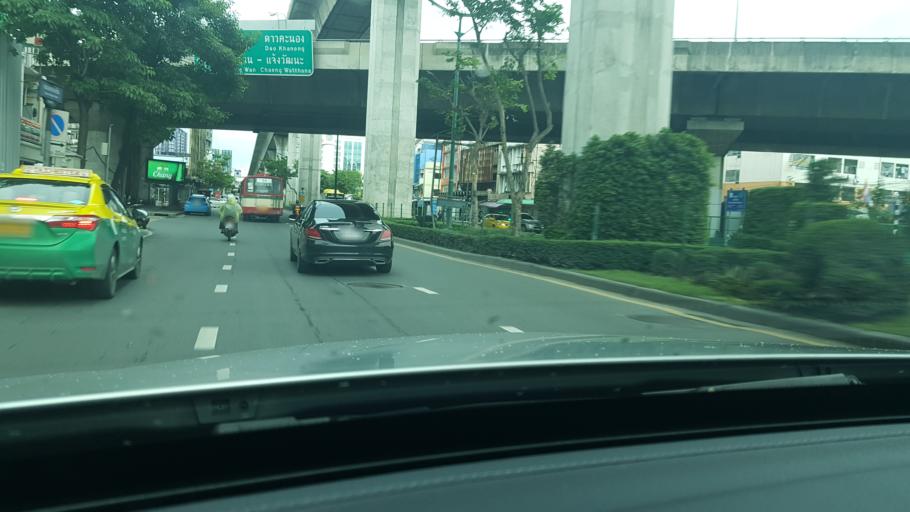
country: TH
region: Bangkok
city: Ratchathewi
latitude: 13.7662
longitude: 100.5389
